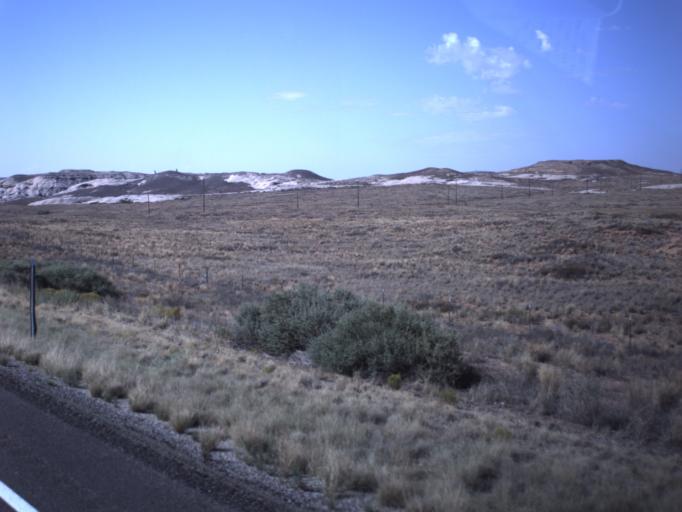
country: US
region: Utah
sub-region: San Juan County
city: Blanding
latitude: 37.3067
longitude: -109.5286
